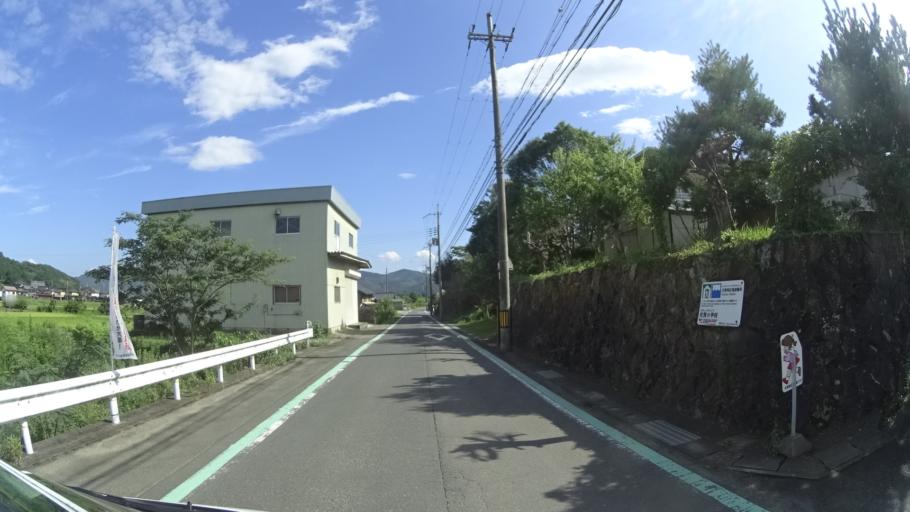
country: JP
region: Kyoto
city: Fukuchiyama
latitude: 35.3201
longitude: 135.1812
